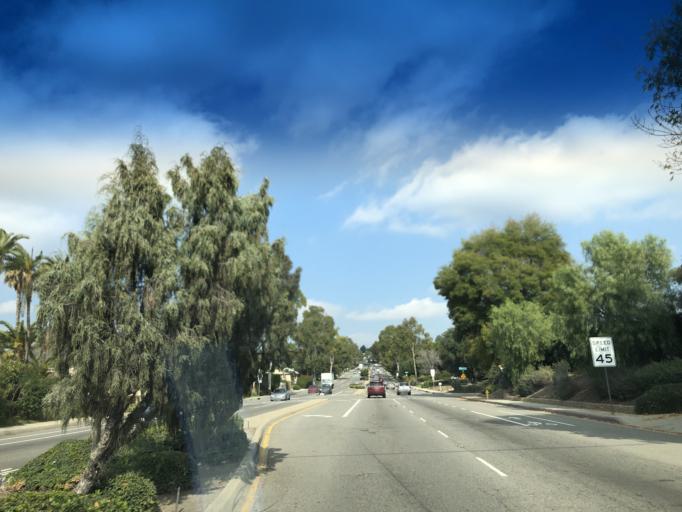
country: US
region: California
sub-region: Los Angeles County
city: East La Mirada
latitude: 33.9507
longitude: -118.0052
